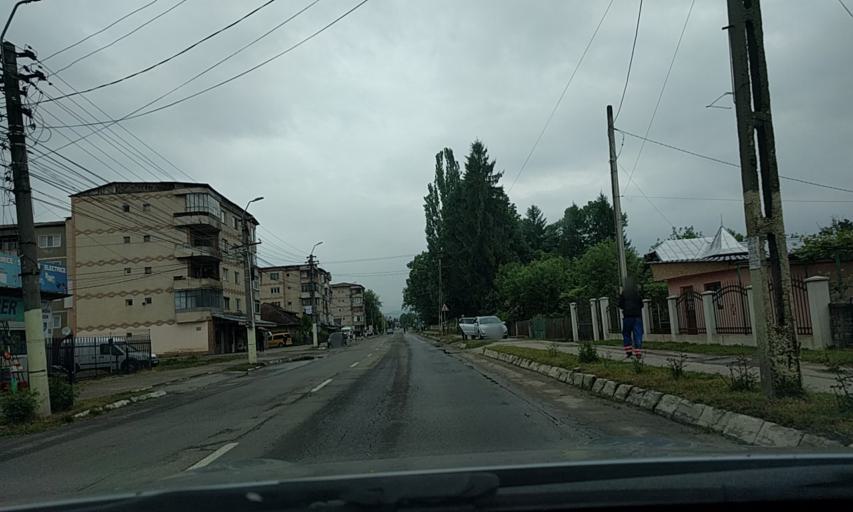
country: RO
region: Dambovita
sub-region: Oras Pucioasa
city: Glodeni
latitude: 45.0588
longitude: 25.4387
